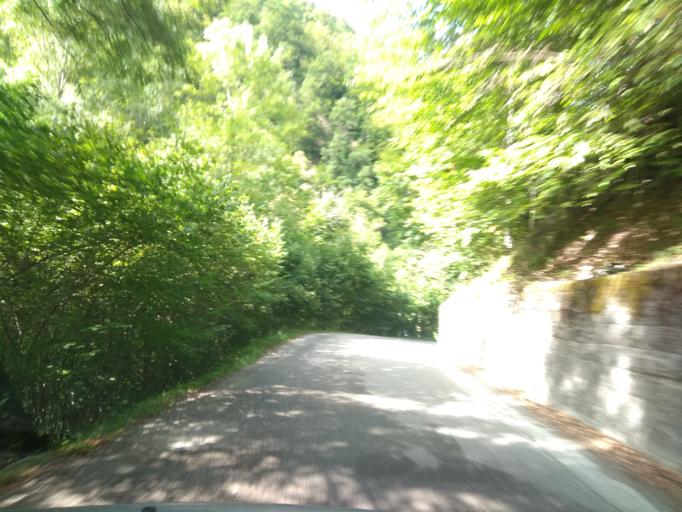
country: ES
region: Catalonia
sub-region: Provincia de Lleida
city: Vielha
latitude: 42.7242
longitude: 0.7270
